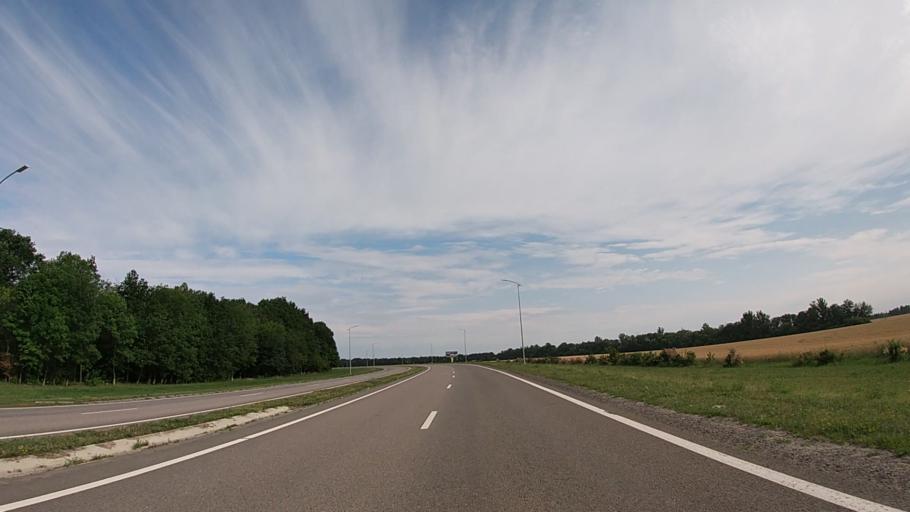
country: RU
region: Belgorod
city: Borisovka
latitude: 50.7580
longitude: 35.9648
